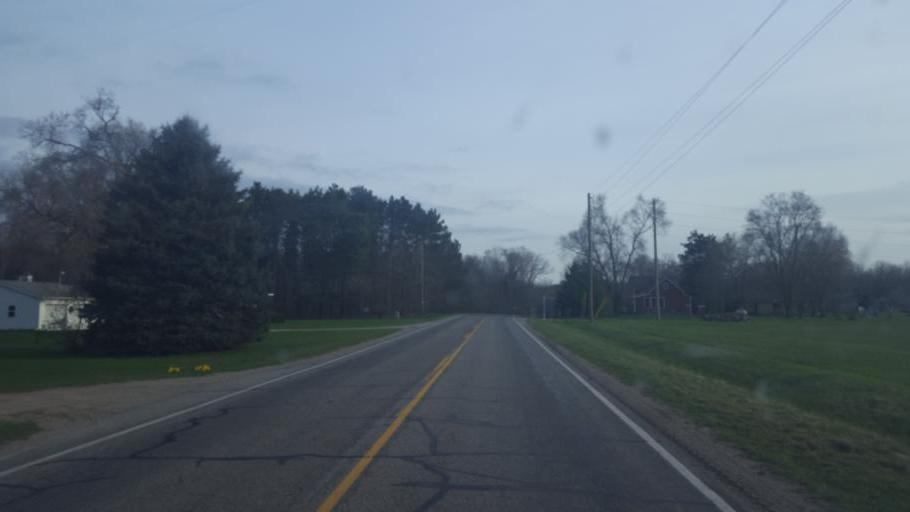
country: US
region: Michigan
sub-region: Isabella County
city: Lake Isabella
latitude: 43.5613
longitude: -84.9865
